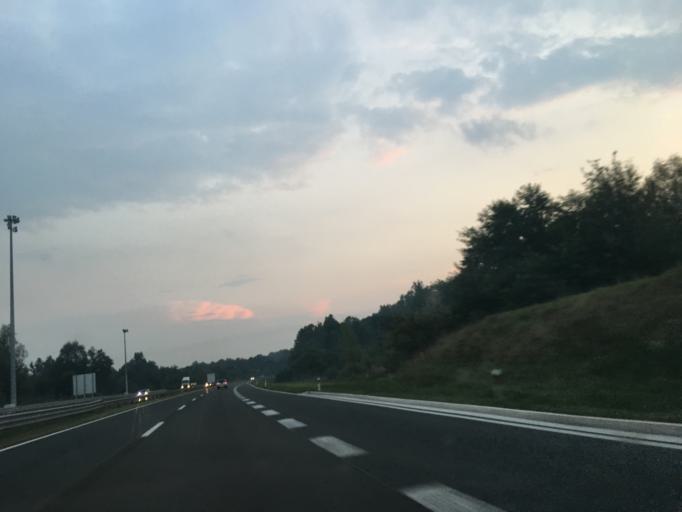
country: HR
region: Karlovacka
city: Ozalj
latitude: 45.4535
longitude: 15.3746
